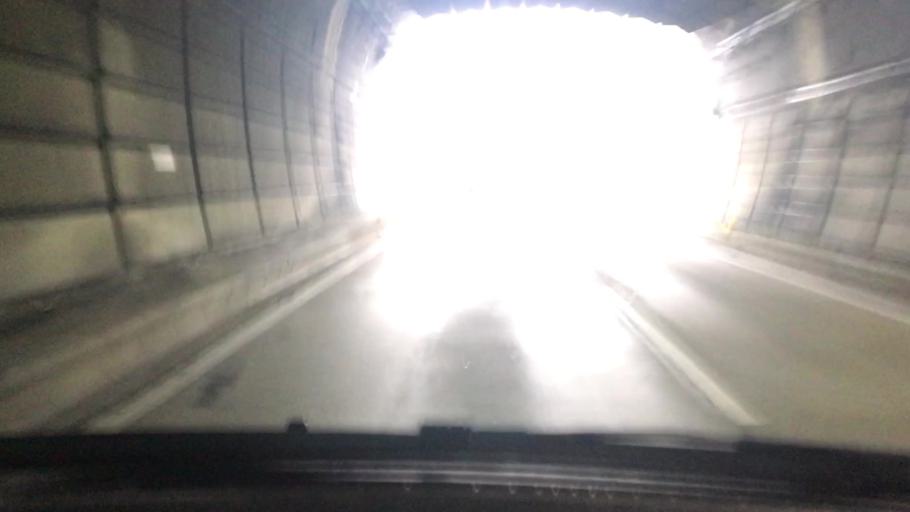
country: JP
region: Hyogo
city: Kobe
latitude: 34.7543
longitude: 135.1619
